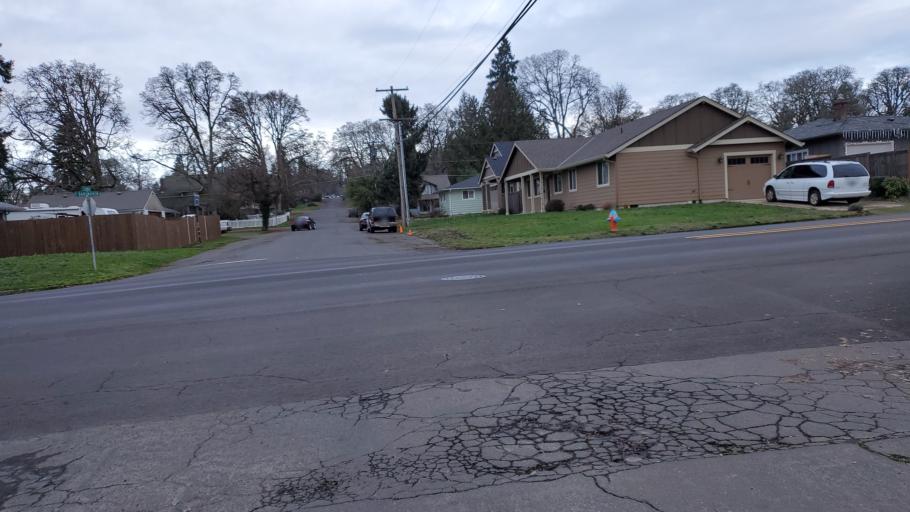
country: US
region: Oregon
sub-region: Clackamas County
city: Gladstone
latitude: 45.3828
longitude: -122.5864
